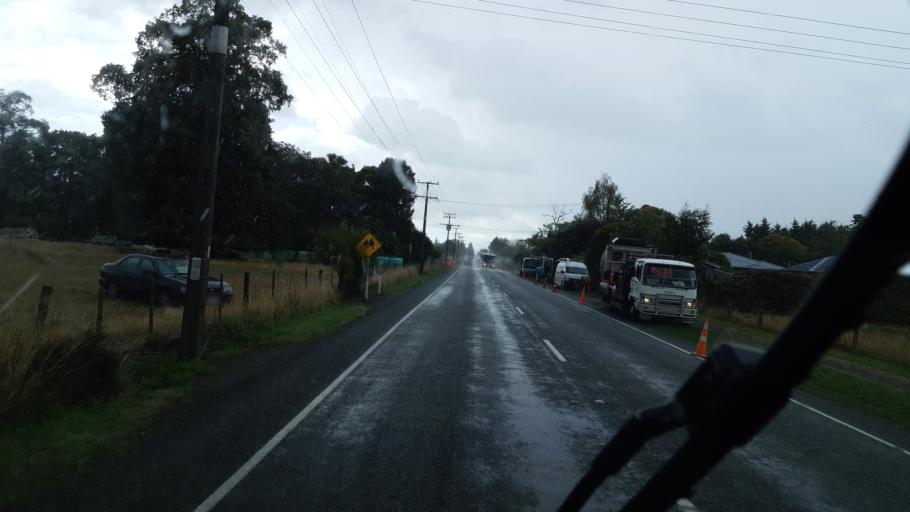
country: NZ
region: Tasman
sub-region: Tasman District
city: Wakefield
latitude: -41.3989
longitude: 173.0599
